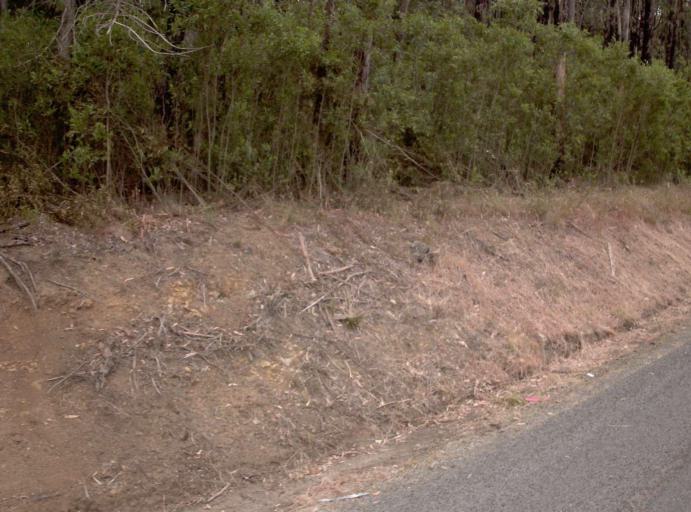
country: AU
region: Victoria
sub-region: Latrobe
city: Moe
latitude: -38.3115
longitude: 146.2682
